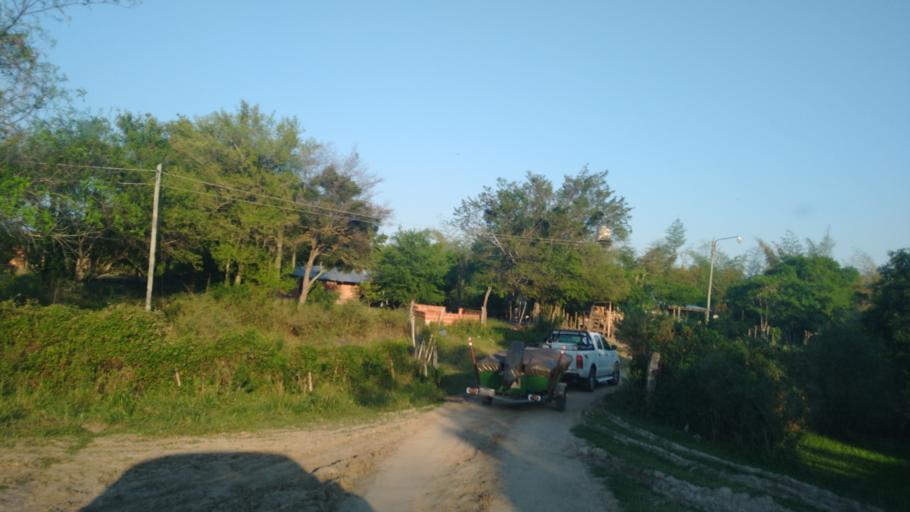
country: PY
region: Neembucu
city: Cerrito
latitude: -27.3714
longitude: -57.6558
